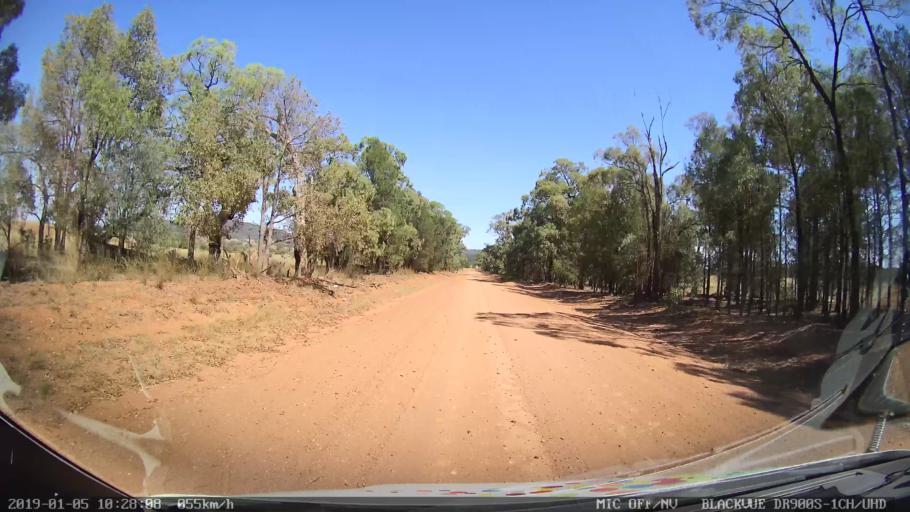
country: AU
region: New South Wales
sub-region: Gilgandra
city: Gilgandra
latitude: -31.5470
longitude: 148.9409
